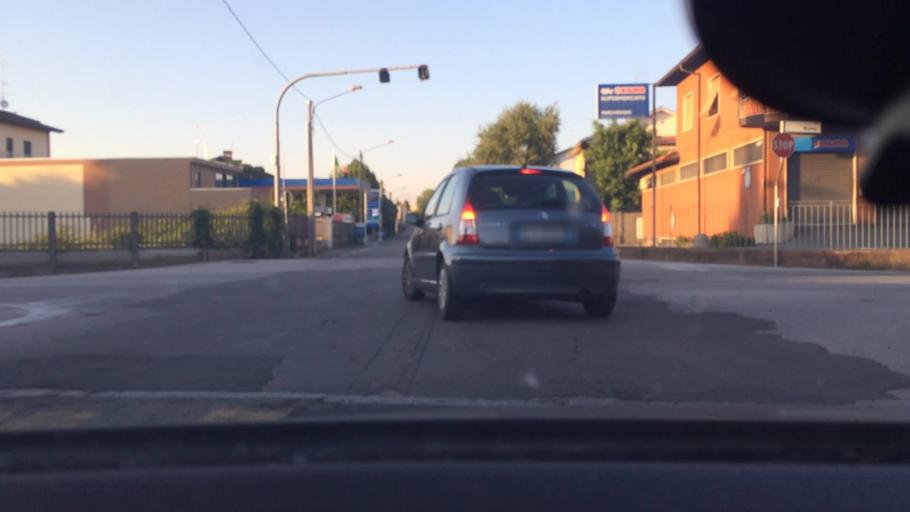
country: IT
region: Lombardy
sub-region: Provincia di Varese
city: Gerenzano
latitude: 45.6425
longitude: 8.9951
